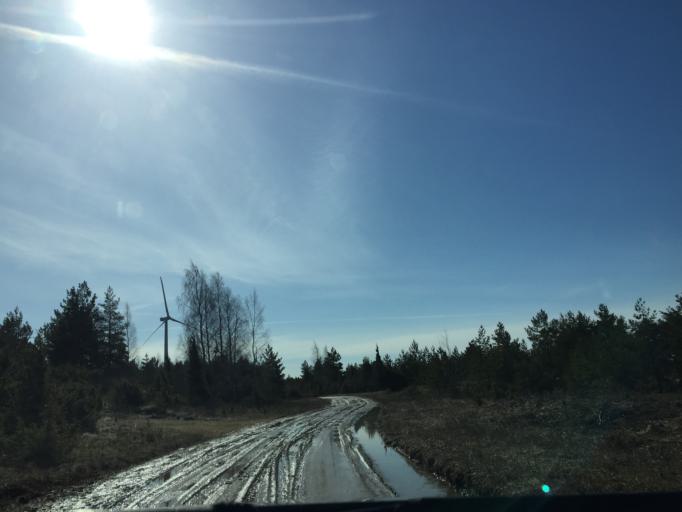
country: EE
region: Laeaene
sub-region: Haapsalu linn
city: Haapsalu
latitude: 58.6451
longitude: 23.5144
